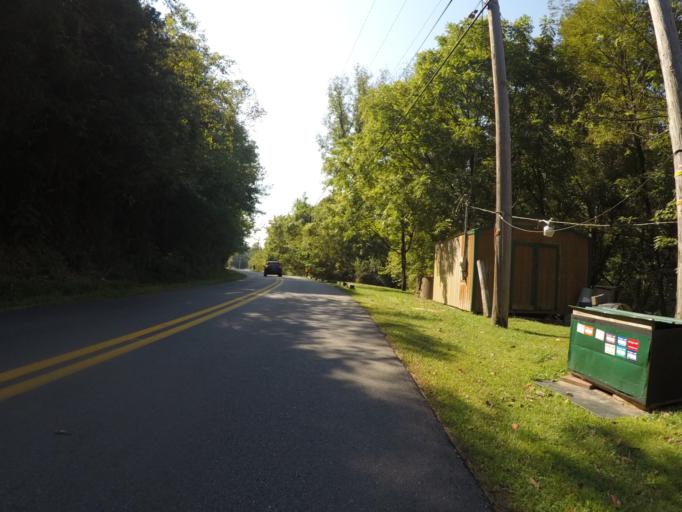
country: US
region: West Virginia
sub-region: Cabell County
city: Barboursville
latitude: 38.3812
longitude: -82.2832
